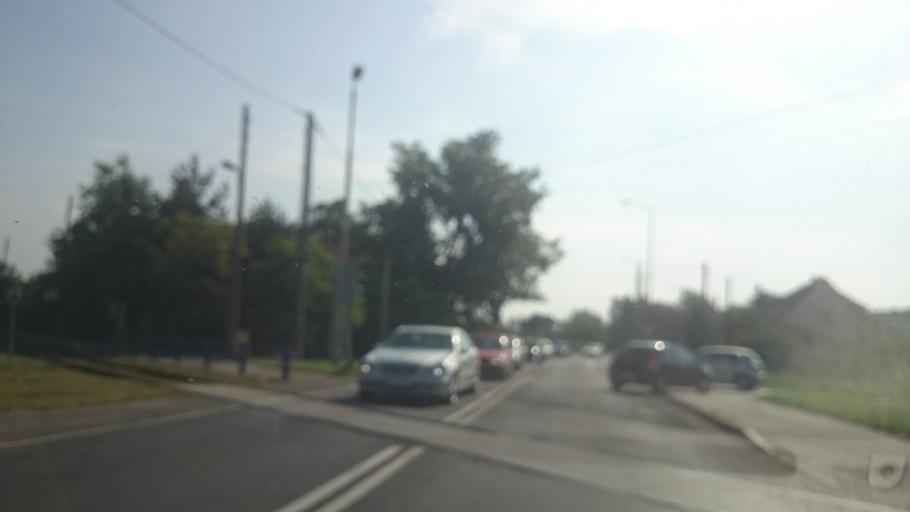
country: PL
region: Opole Voivodeship
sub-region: Powiat opolski
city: Opole
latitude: 50.6729
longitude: 17.9870
